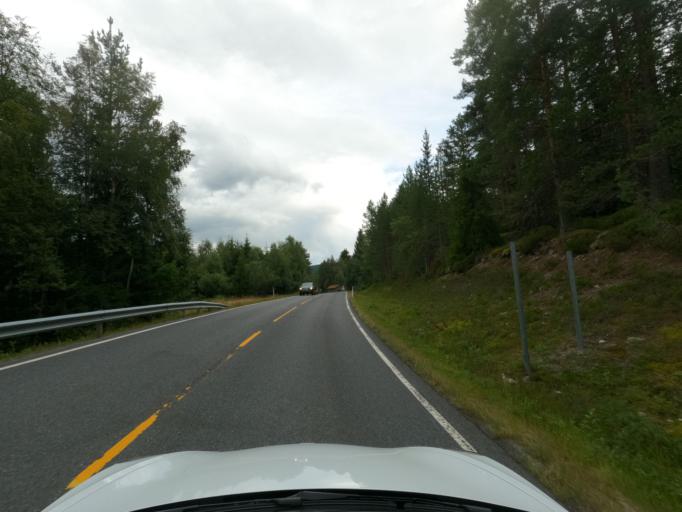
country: NO
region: Telemark
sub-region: Notodden
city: Notodden
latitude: 59.7305
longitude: 9.3470
